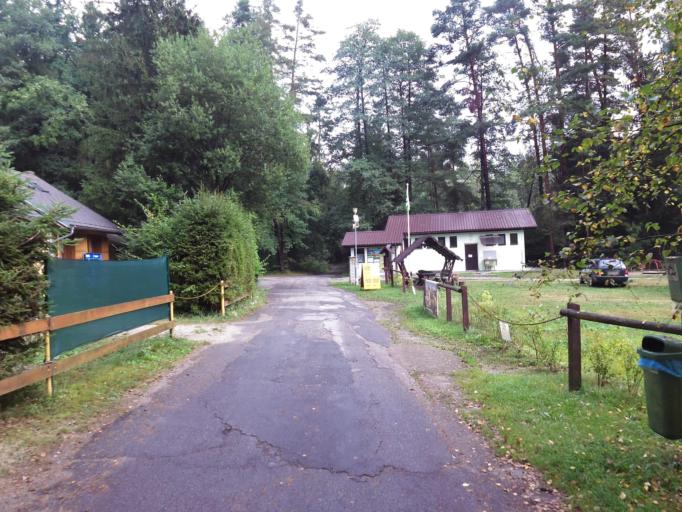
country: CZ
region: Jihocesky
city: Chlum u Trebone
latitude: 48.9841
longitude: 14.9608
